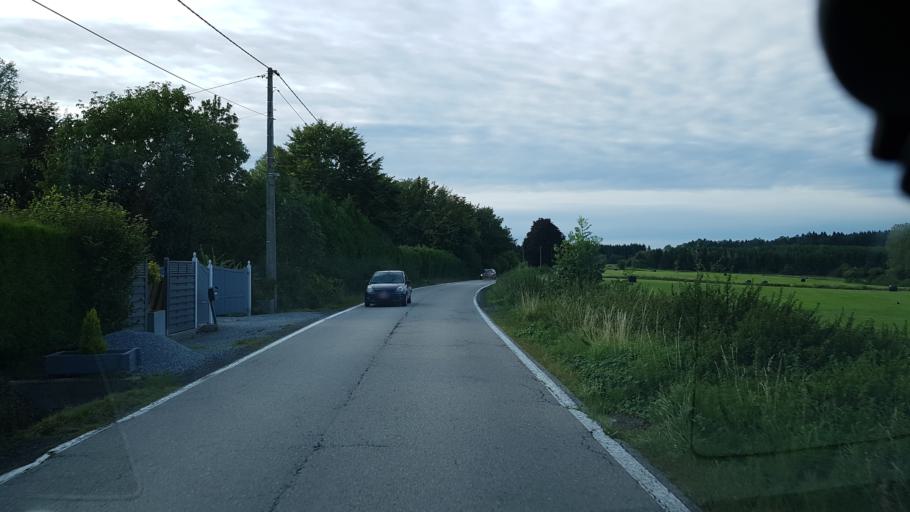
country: BE
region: Wallonia
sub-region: Province de Liege
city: Theux
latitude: 50.5000
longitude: 5.7675
